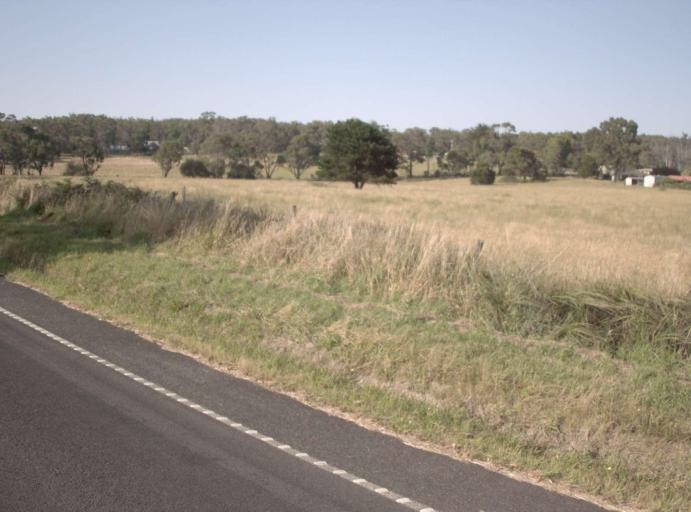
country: AU
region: Victoria
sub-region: Latrobe
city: Morwell
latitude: -38.3826
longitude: 146.2773
